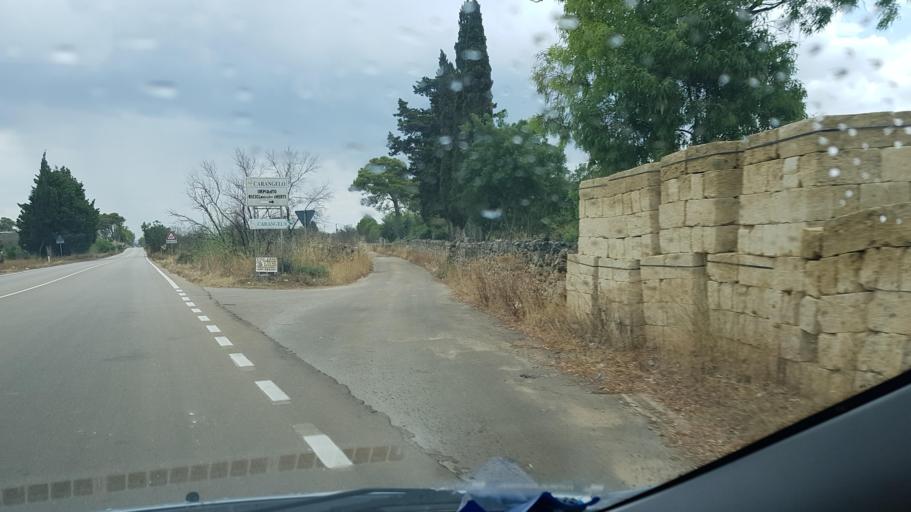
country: IT
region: Apulia
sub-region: Provincia di Lecce
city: Acquarica del Capo
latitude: 39.9269
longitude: 18.2355
